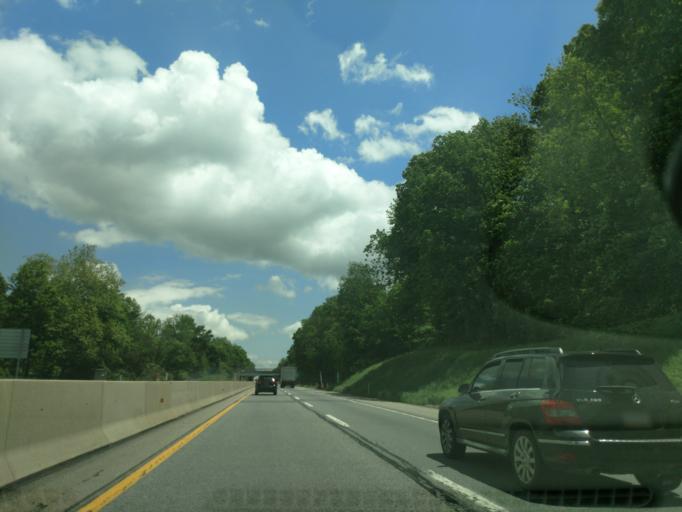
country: US
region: Pennsylvania
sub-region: Lancaster County
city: Swartzville
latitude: 40.2137
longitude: -76.0614
